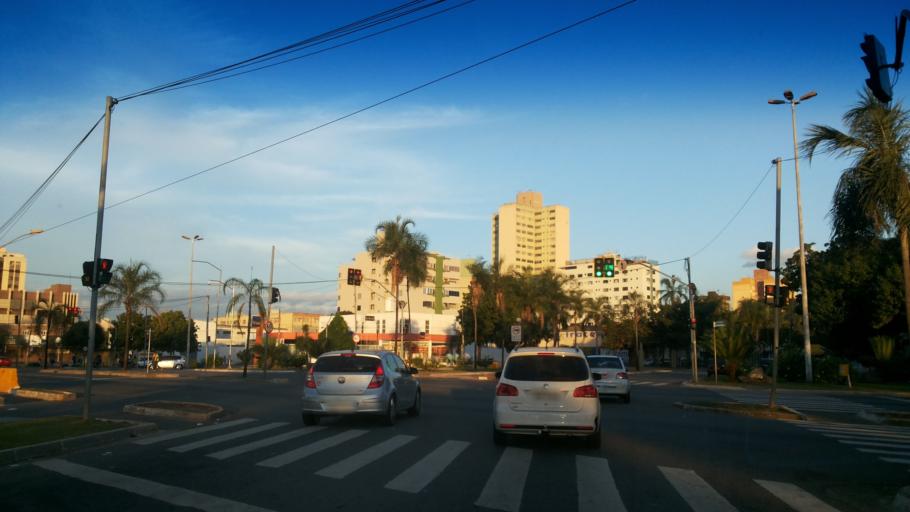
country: BR
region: Goias
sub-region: Goiania
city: Goiania
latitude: -16.6642
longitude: -49.2620
